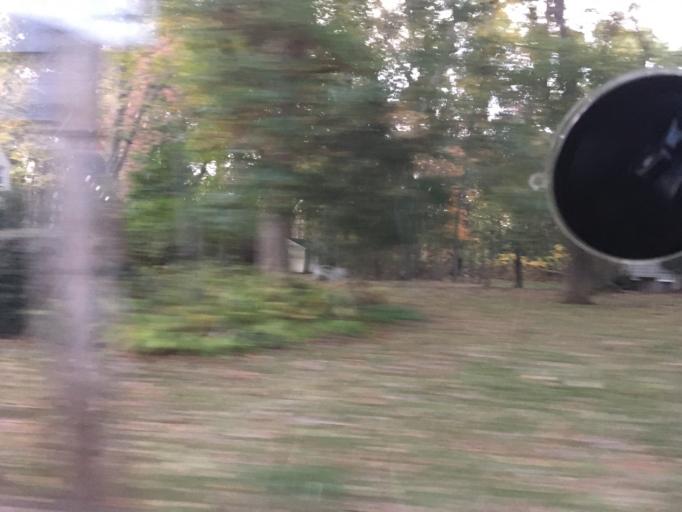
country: US
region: Rhode Island
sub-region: Kent County
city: East Greenwich
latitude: 41.6485
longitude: -71.5005
